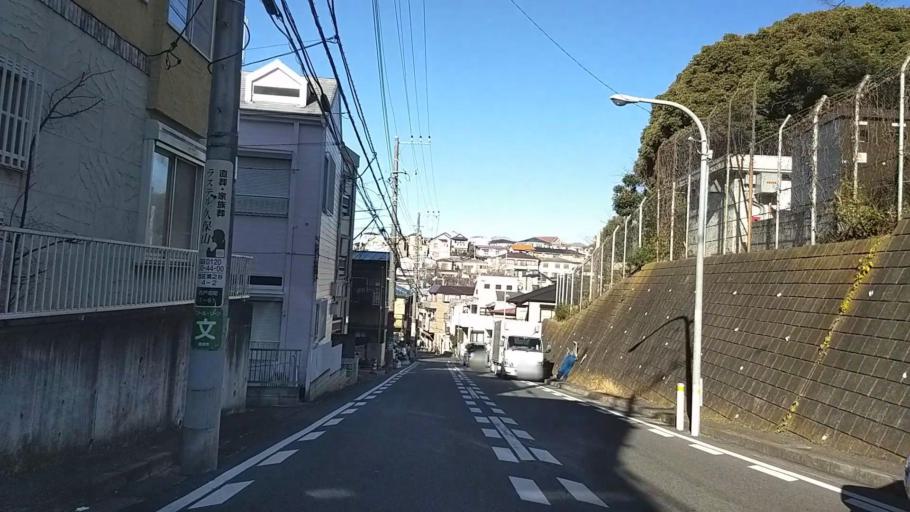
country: JP
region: Kanagawa
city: Yokohama
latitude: 35.4471
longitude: 139.6219
